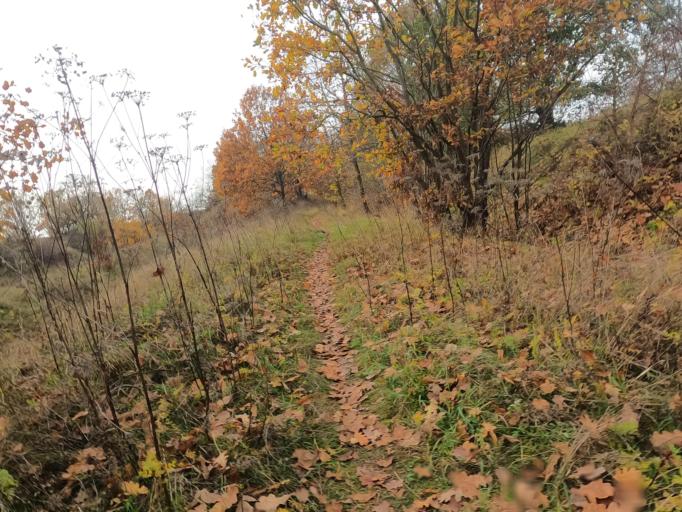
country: PL
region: Pomeranian Voivodeship
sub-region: Powiat starogardzki
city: Starogard Gdanski
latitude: 53.9726
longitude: 18.5110
